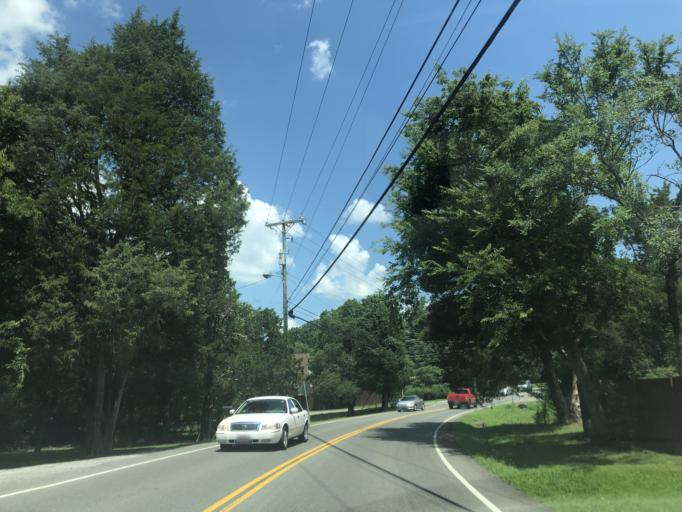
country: US
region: Tennessee
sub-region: Wilson County
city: Green Hill
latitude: 36.1541
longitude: -86.5863
